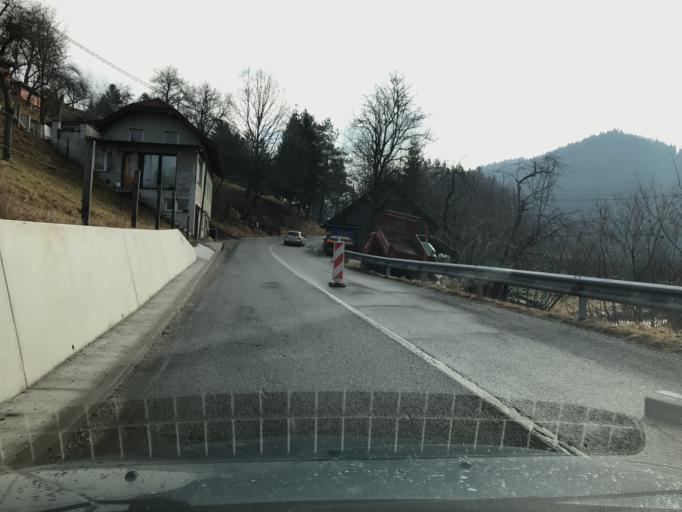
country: SI
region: Lukovica
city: Lukovica pri Domzalah
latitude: 46.2180
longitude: 14.7005
